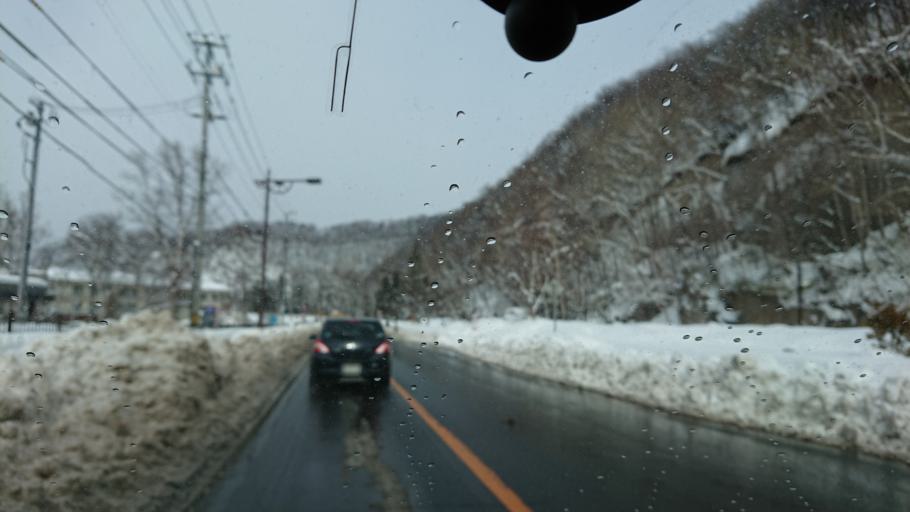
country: JP
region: Hokkaido
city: Sapporo
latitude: 42.9803
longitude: 141.3435
